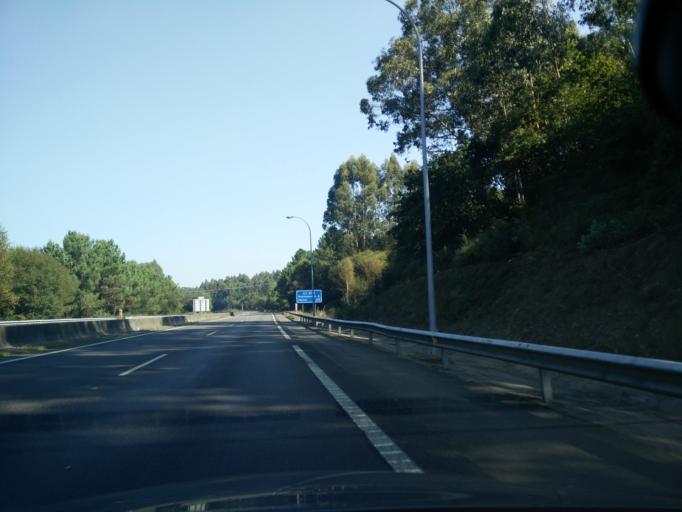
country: ES
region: Galicia
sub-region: Provincia da Coruna
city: Mino
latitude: 43.3794
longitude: -8.1814
